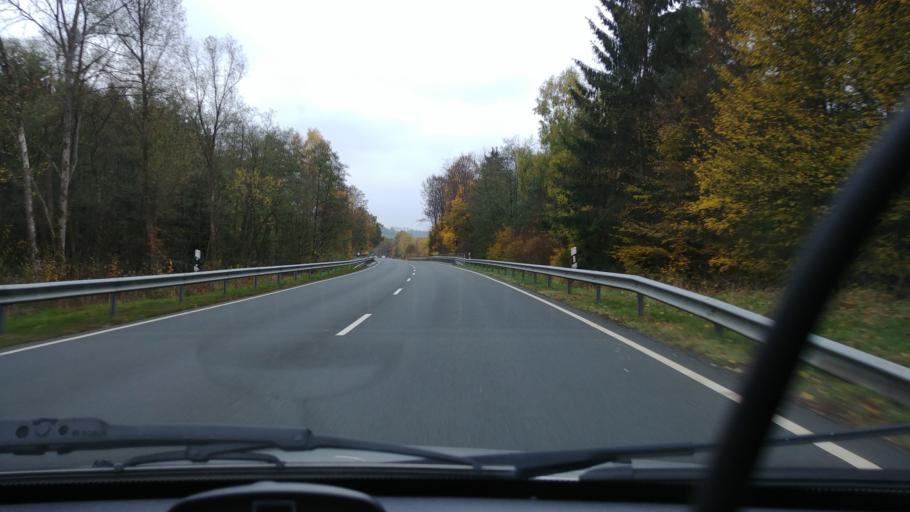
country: DE
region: Rheinland-Pfalz
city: Unnau
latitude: 50.6557
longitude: 7.8852
